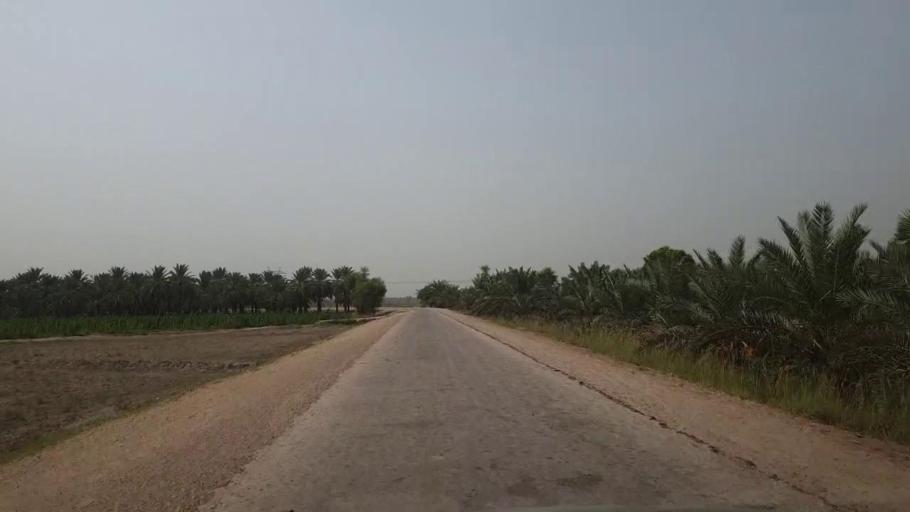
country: PK
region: Sindh
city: Gambat
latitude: 27.4182
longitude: 68.5481
